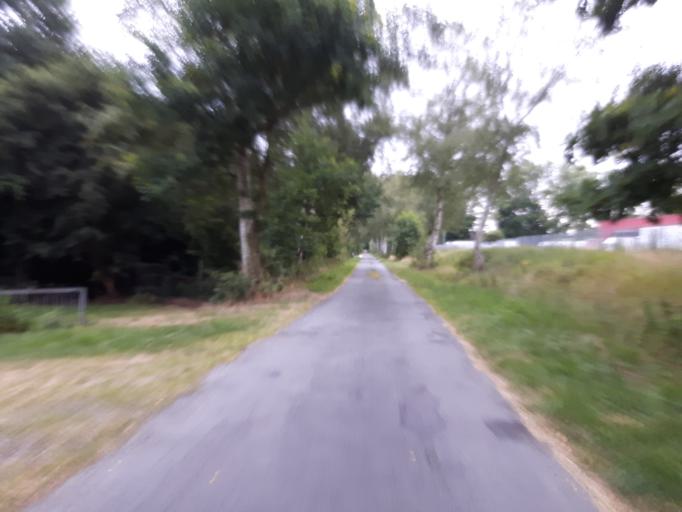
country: DE
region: Lower Saxony
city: Stuhr
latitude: 53.0200
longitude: 8.6959
